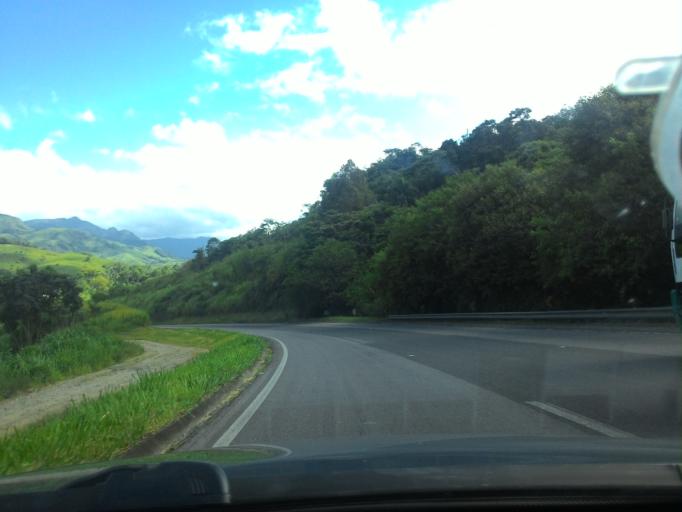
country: BR
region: Sao Paulo
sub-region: Cajati
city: Cajati
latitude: -24.7956
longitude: -48.2147
